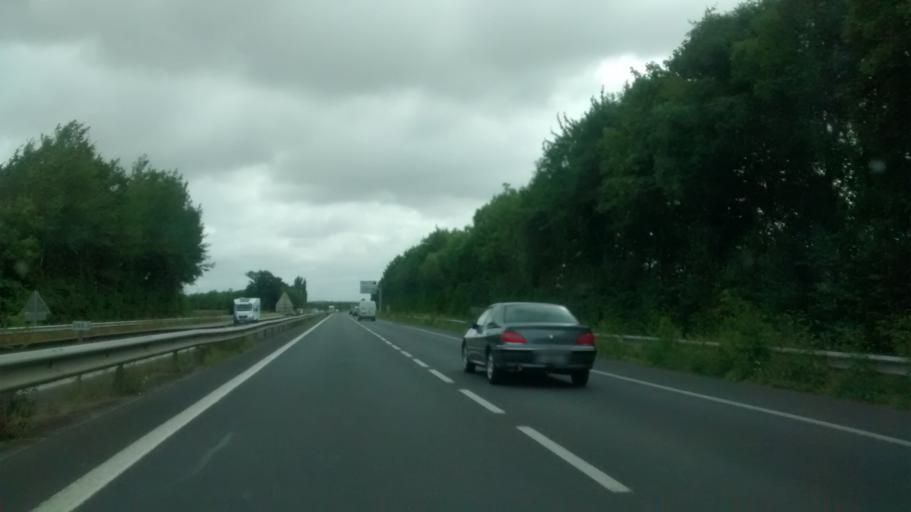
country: FR
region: Lower Normandy
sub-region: Departement du Calvados
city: Villers-Bocage
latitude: 49.1085
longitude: -0.6003
